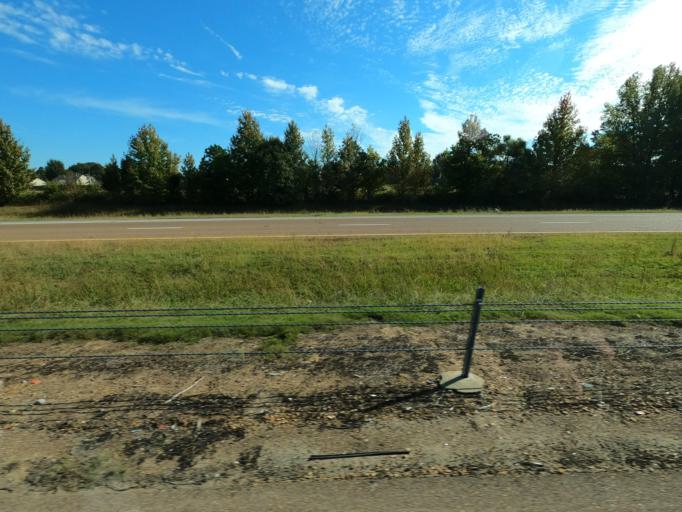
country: US
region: Tennessee
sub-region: Shelby County
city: Arlington
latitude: 35.2748
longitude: -89.6792
